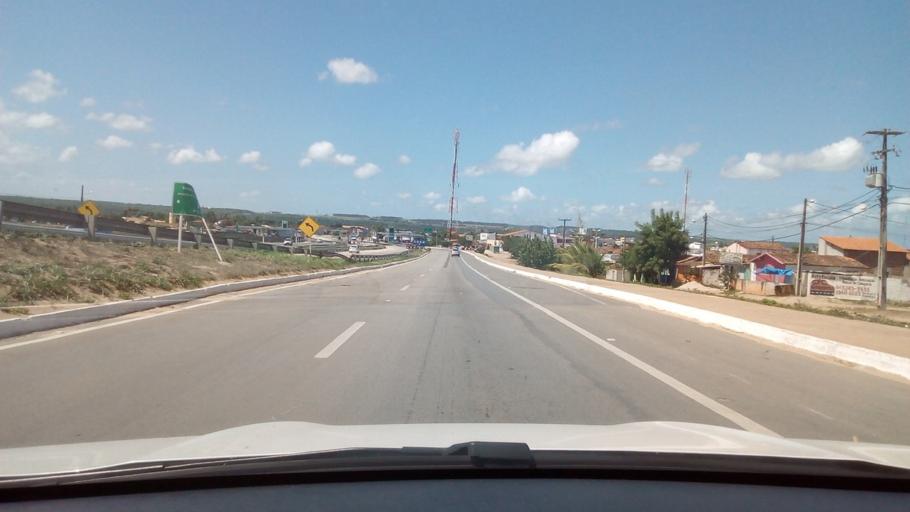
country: BR
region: Rio Grande do Norte
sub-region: Goianinha
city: Goianinha
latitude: -6.2749
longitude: -35.2070
